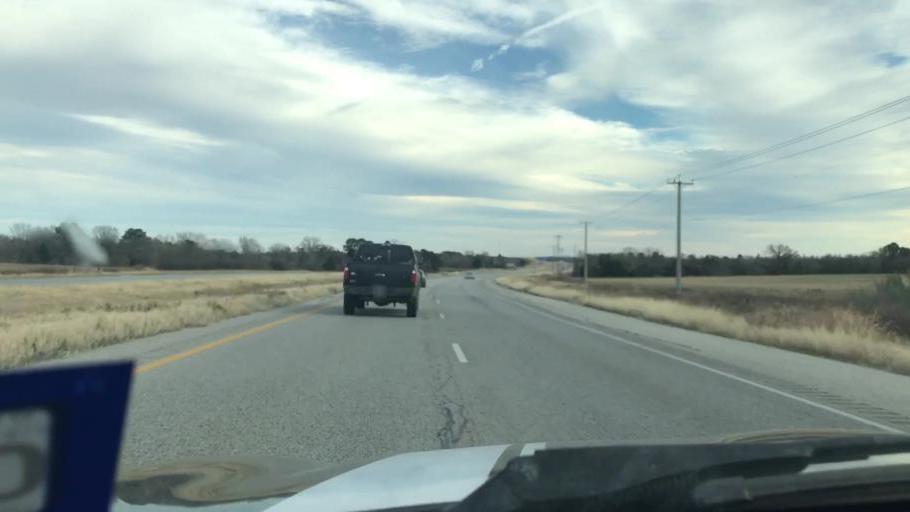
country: US
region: Texas
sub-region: Bastrop County
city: Elgin
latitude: 30.3208
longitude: -97.3185
